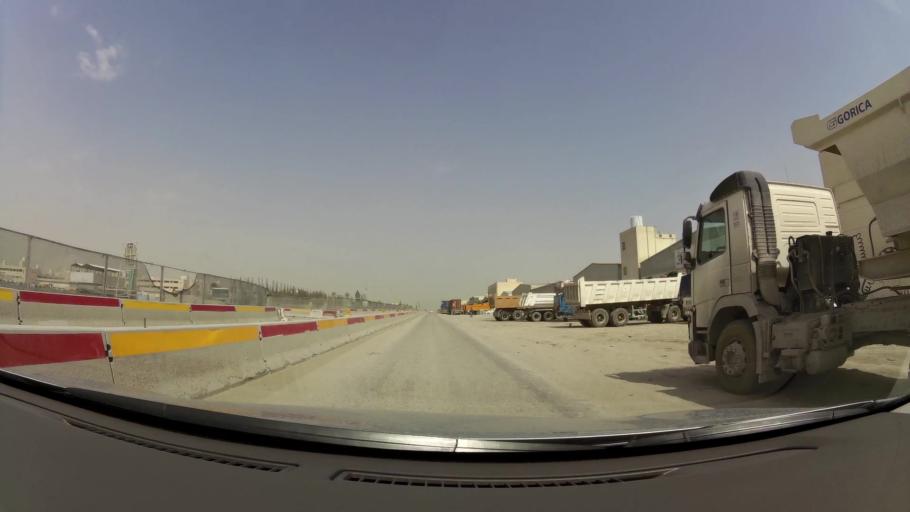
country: QA
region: Al Wakrah
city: Al Wukayr
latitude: 25.1654
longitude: 51.4533
